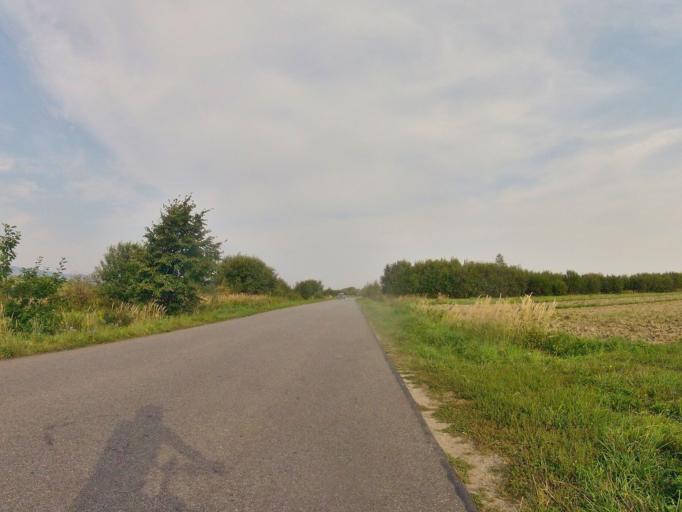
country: PL
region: Subcarpathian Voivodeship
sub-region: Powiat jasielski
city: Nowy Zmigrod
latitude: 49.6236
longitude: 21.5124
